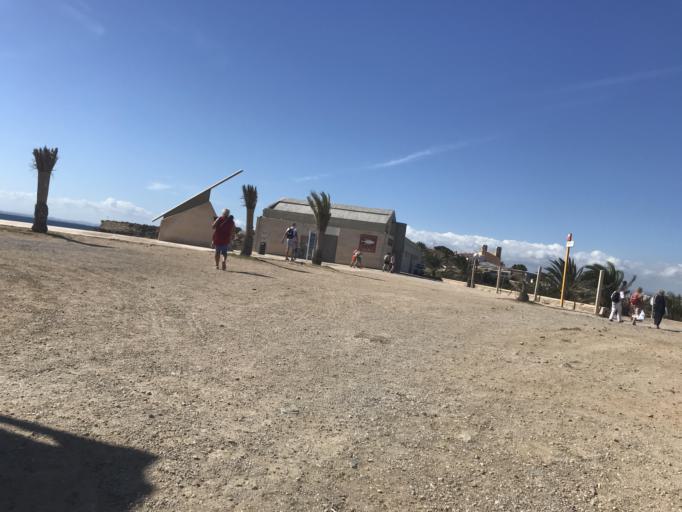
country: ES
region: Valencia
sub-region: Provincia de Alicante
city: Santa Pola
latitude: 38.1660
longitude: -0.4777
